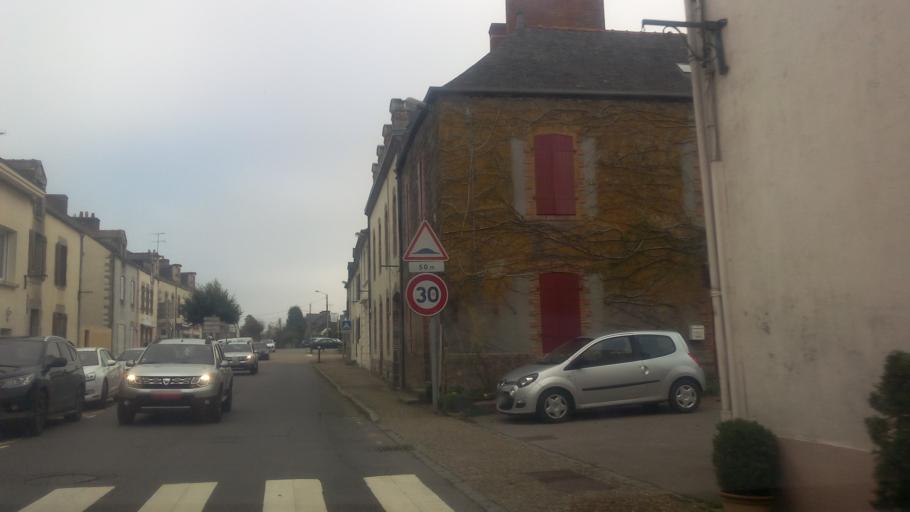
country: FR
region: Brittany
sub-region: Departement du Morbihan
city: Peillac
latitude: 47.7134
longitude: -2.2168
